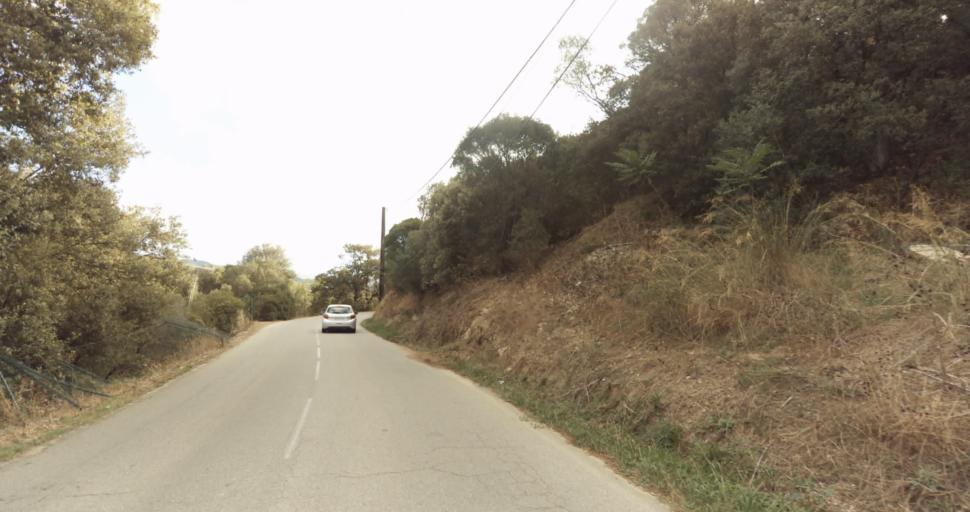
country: FR
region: Corsica
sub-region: Departement de la Corse-du-Sud
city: Ajaccio
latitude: 41.9310
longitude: 8.7188
